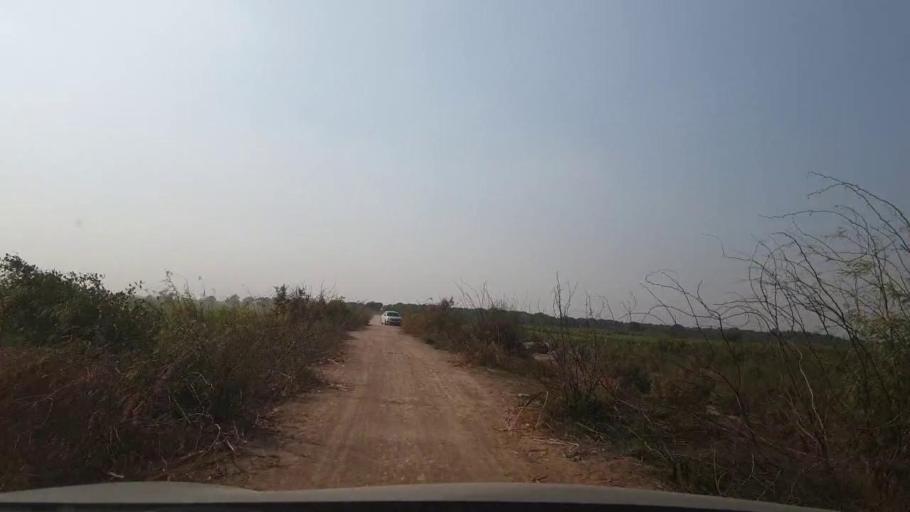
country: PK
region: Sindh
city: Tando Allahyar
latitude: 25.5933
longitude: 68.8234
